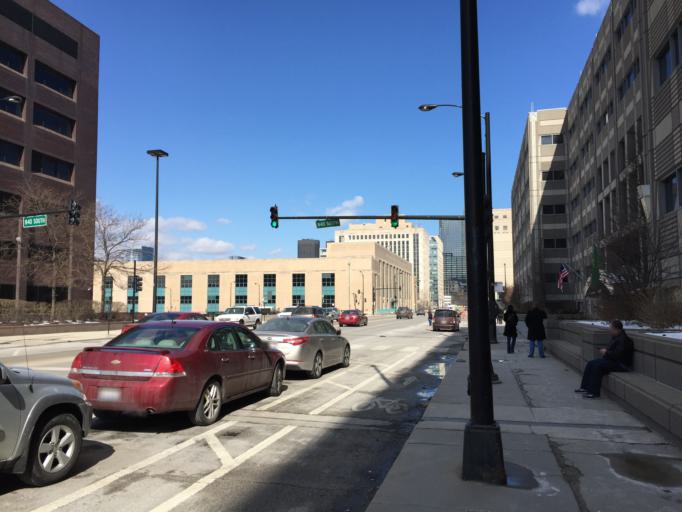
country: US
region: Illinois
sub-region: Cook County
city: Chicago
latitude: 41.8708
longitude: -87.6392
